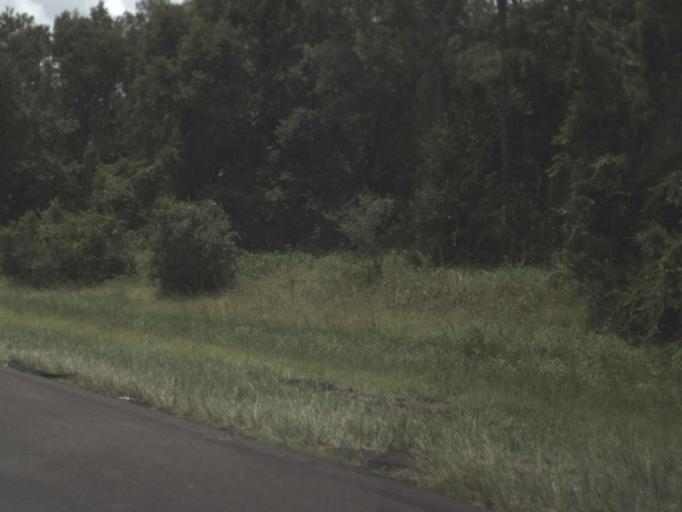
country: US
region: Florida
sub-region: Pasco County
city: San Antonio
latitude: 28.3795
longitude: -82.3196
